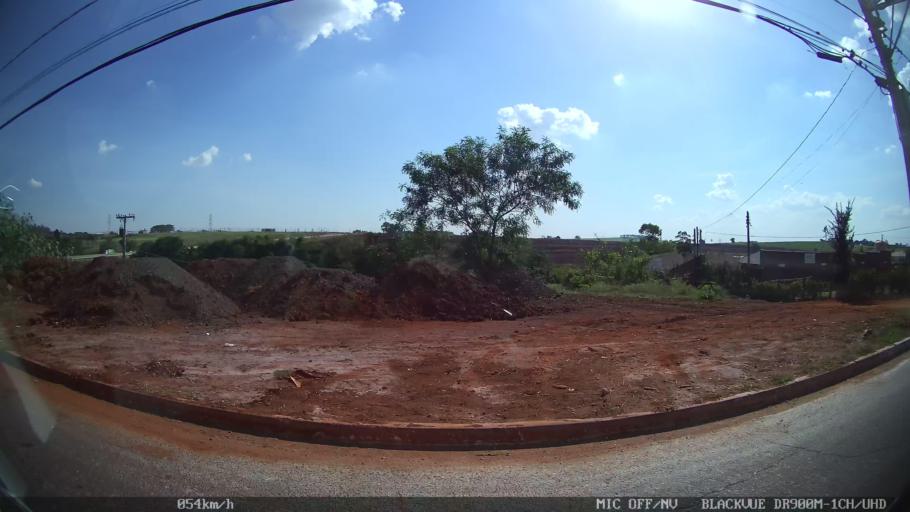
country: BR
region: Sao Paulo
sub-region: Ribeirao Preto
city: Ribeirao Preto
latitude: -21.2041
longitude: -47.8589
